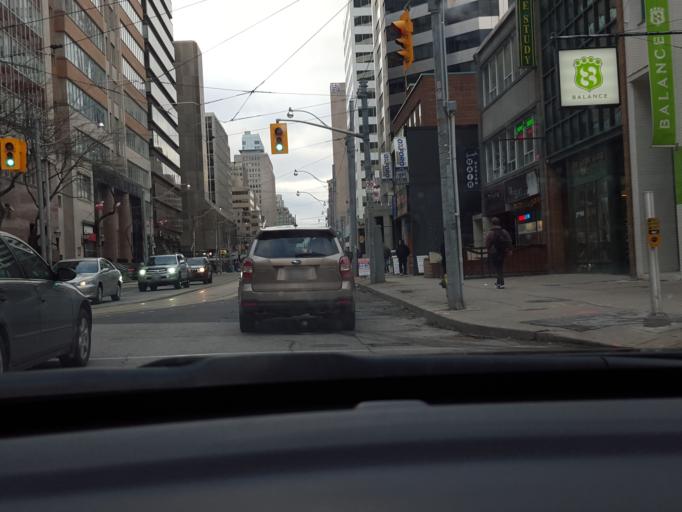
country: CA
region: Ontario
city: Toronto
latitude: 43.6887
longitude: -79.3914
